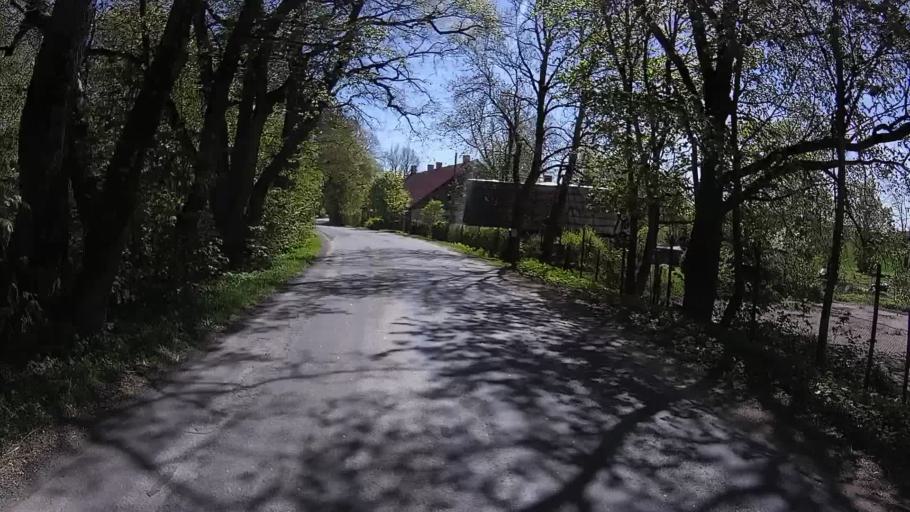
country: EE
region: Harju
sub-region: Raasiku vald
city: Raasiku
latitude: 59.1040
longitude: 25.1677
